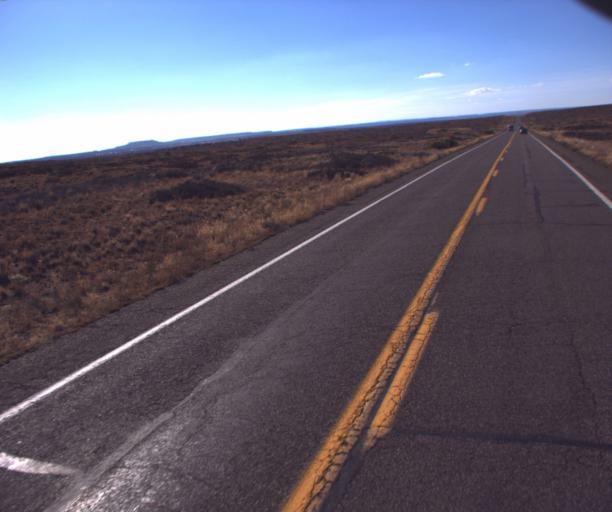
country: US
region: Arizona
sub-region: Coconino County
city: Kaibito
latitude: 36.6120
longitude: -111.0168
